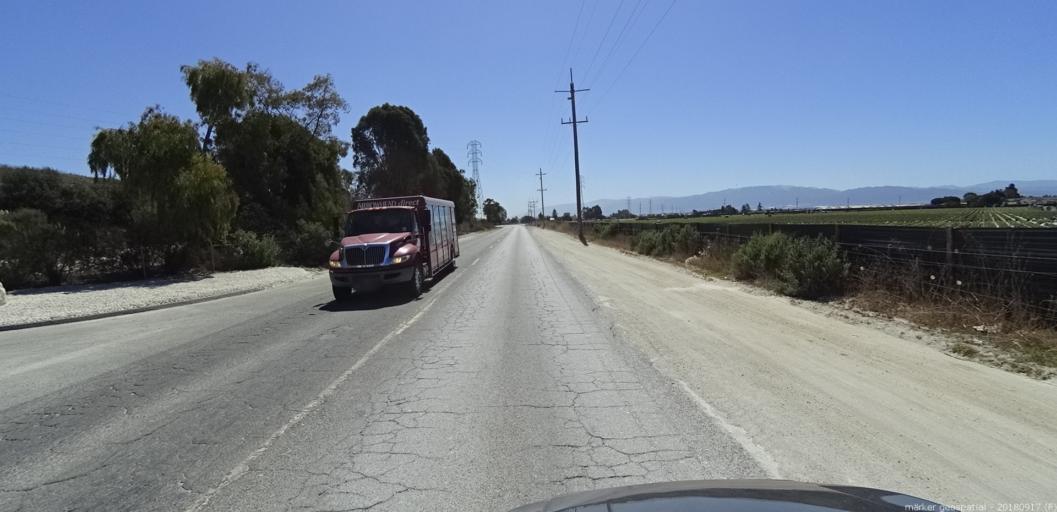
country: US
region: California
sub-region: Monterey County
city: Prunedale
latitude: 36.7457
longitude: -121.6046
